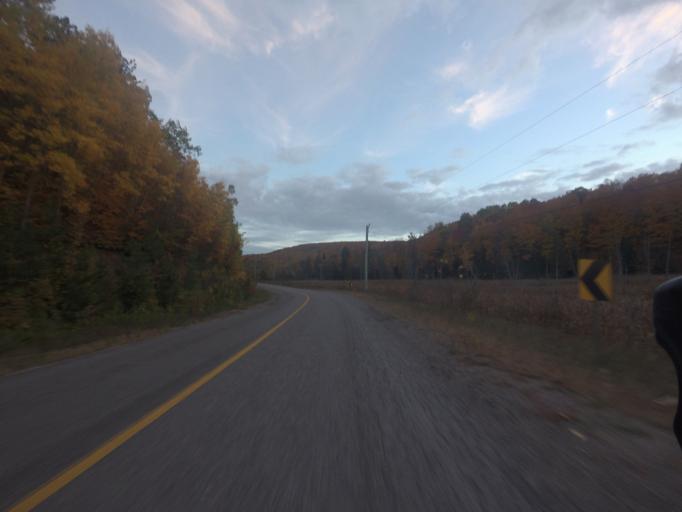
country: CA
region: Ontario
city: Renfrew
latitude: 45.3618
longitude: -76.9667
